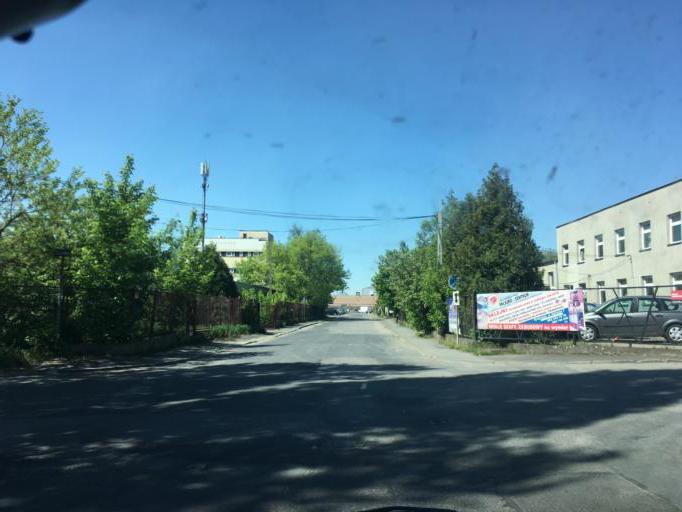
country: PL
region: Kujawsko-Pomorskie
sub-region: Powiat bydgoski
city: Osielsko
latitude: 53.1251
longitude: 18.0734
